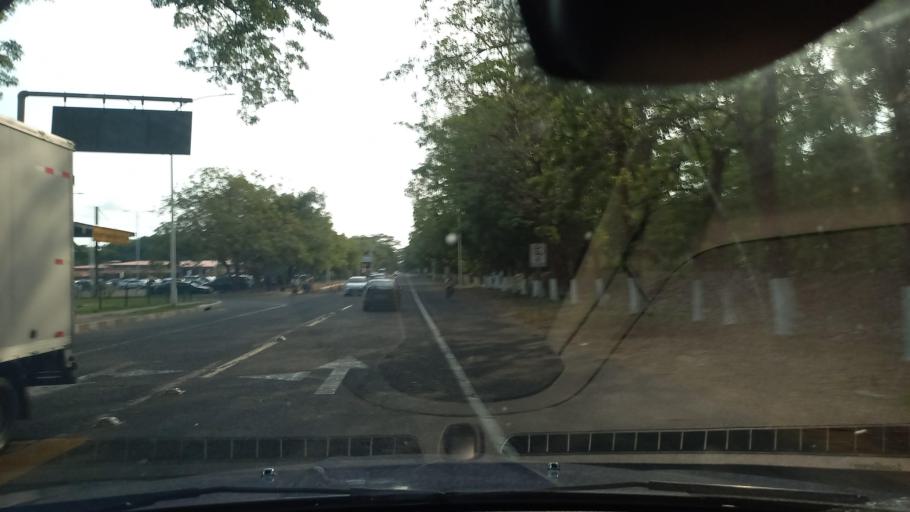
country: SV
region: La Paz
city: El Rosario
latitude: 13.4480
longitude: -89.0557
